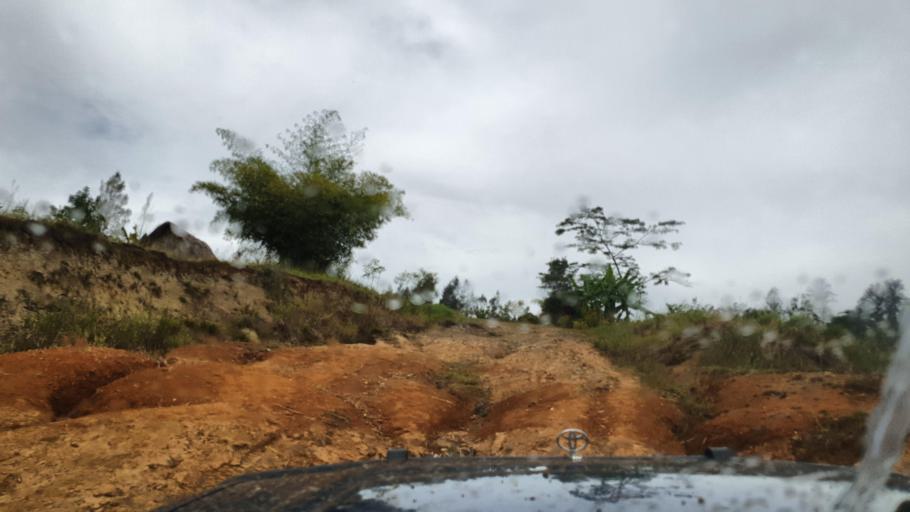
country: PG
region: Jiwaka
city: Minj
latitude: -5.9524
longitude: 144.7772
